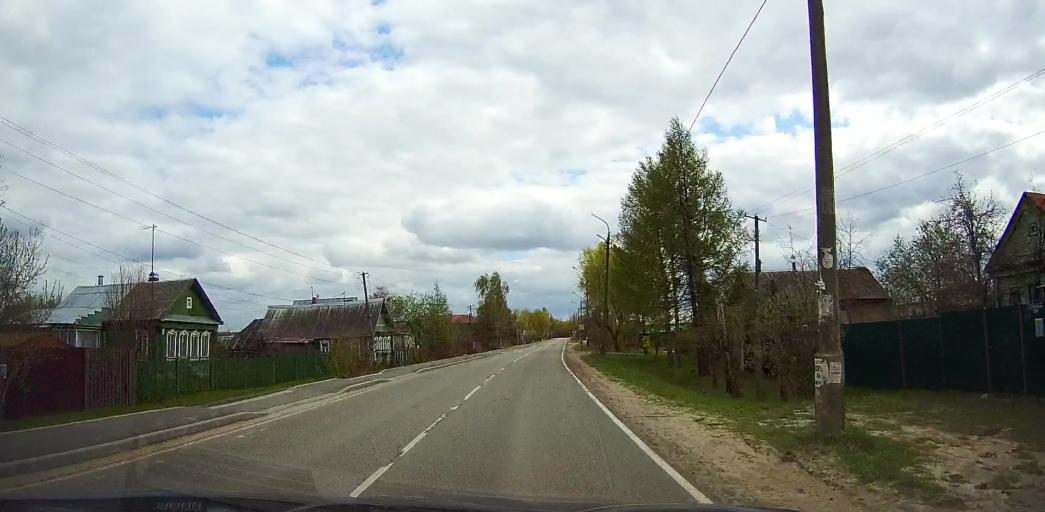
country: RU
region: Moskovskaya
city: Imeni Tsyurupy
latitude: 55.4922
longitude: 38.6720
